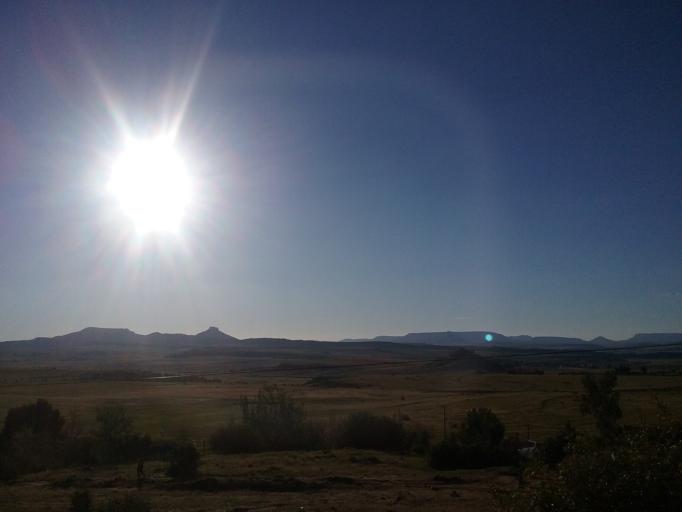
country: LS
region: Mohale's Hoek District
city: Mohale's Hoek
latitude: -30.1885
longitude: 27.4175
